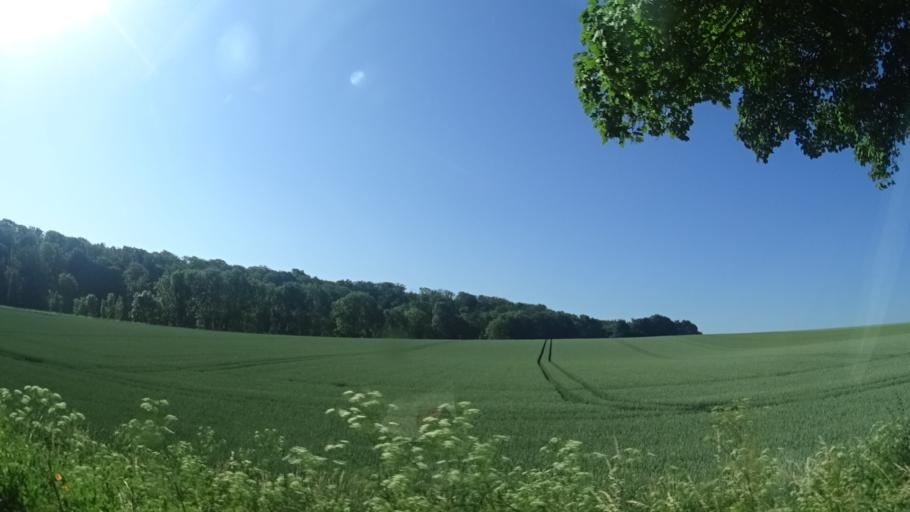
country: DE
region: Lower Saxony
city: Haverlah
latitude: 52.0795
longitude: 10.1975
